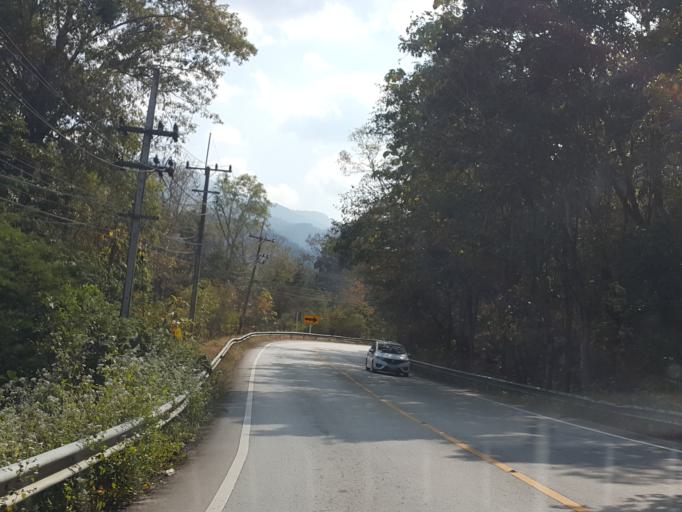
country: TH
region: Chiang Mai
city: Hot
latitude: 18.2094
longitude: 98.4474
